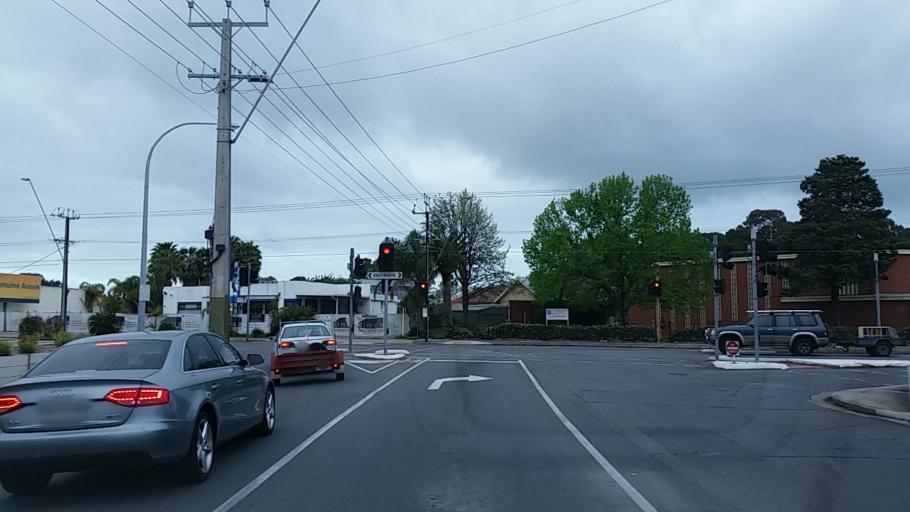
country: AU
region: South Australia
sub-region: Charles Sturt
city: Findon
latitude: -34.9267
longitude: 138.5351
